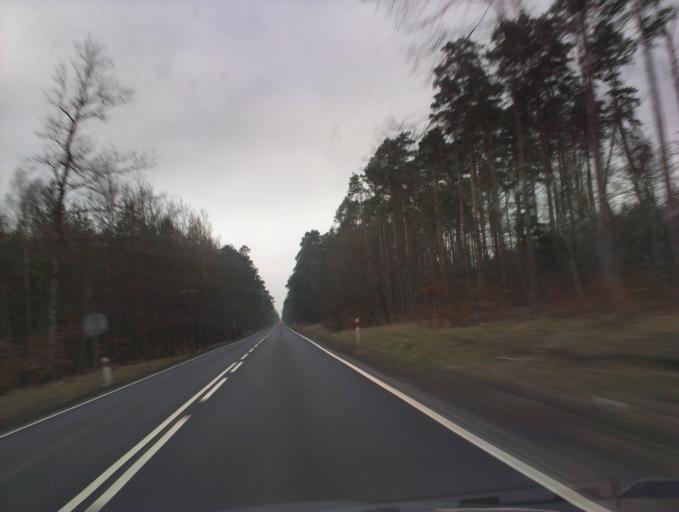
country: PL
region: Greater Poland Voivodeship
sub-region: Powiat zlotowski
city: Jastrowie
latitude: 53.3822
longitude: 16.7935
